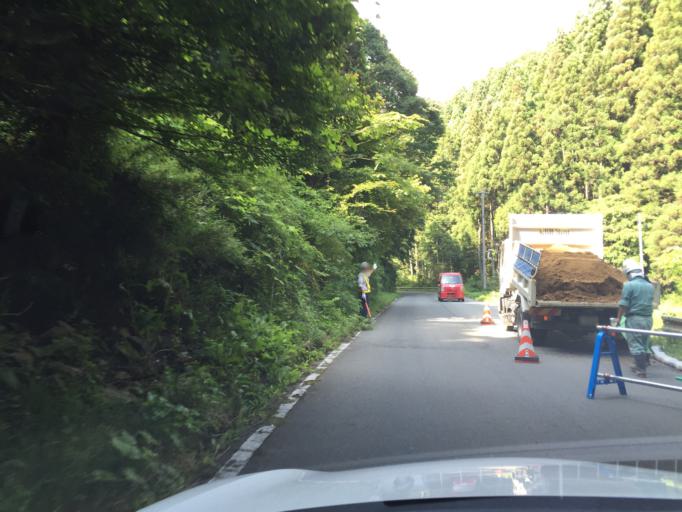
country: JP
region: Fukushima
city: Iwaki
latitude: 36.9965
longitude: 140.7106
